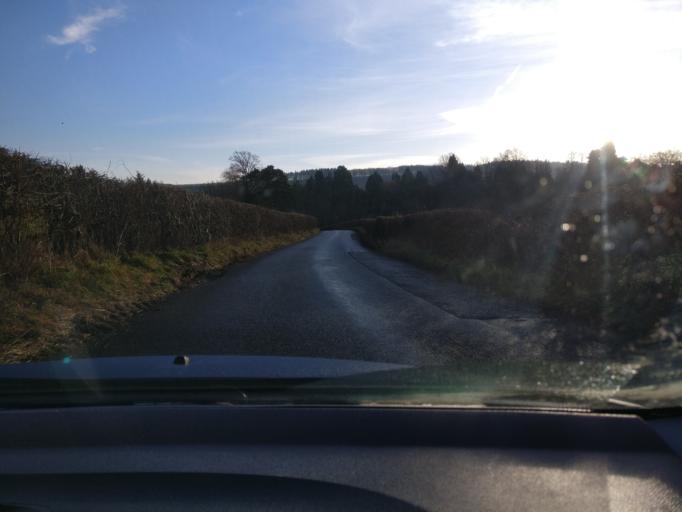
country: GB
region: Scotland
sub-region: The Scottish Borders
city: Hawick
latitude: 55.4437
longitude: -2.7434
